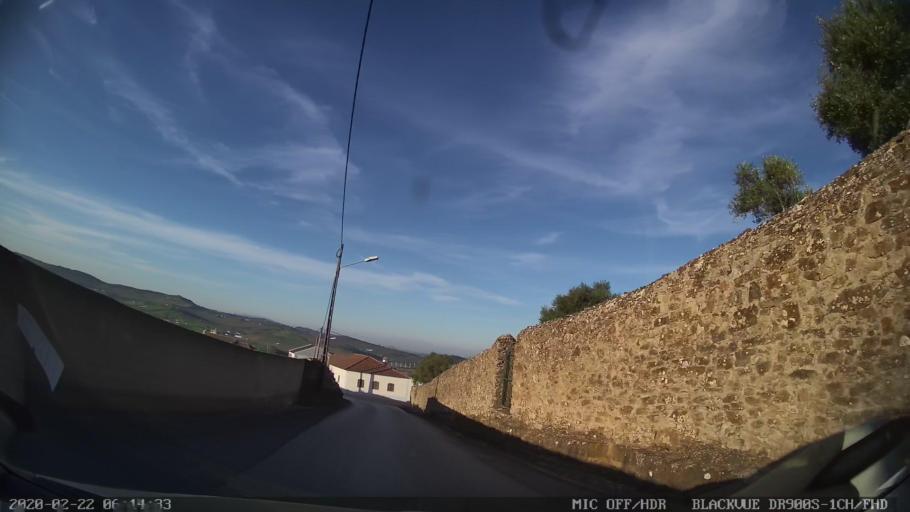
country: PT
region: Lisbon
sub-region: Vila Franca de Xira
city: Vila Franca de Xira
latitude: 38.9840
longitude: -9.0150
